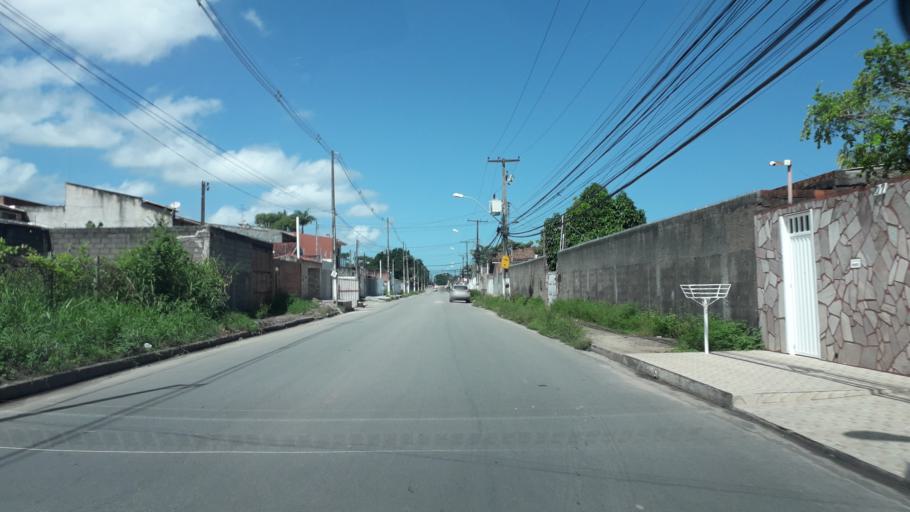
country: BR
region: Alagoas
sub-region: Satuba
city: Satuba
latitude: -9.5566
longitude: -35.7844
